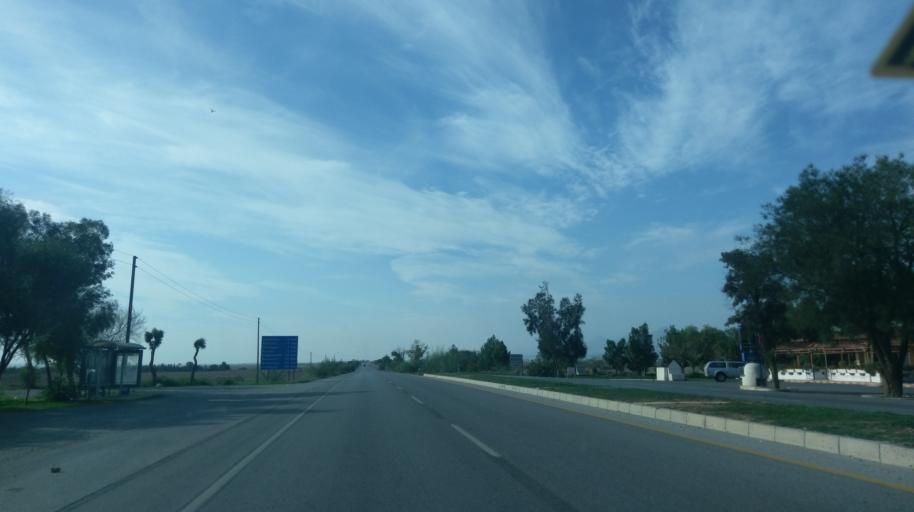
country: CY
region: Larnaka
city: Athienou
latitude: 35.2087
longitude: 33.5815
